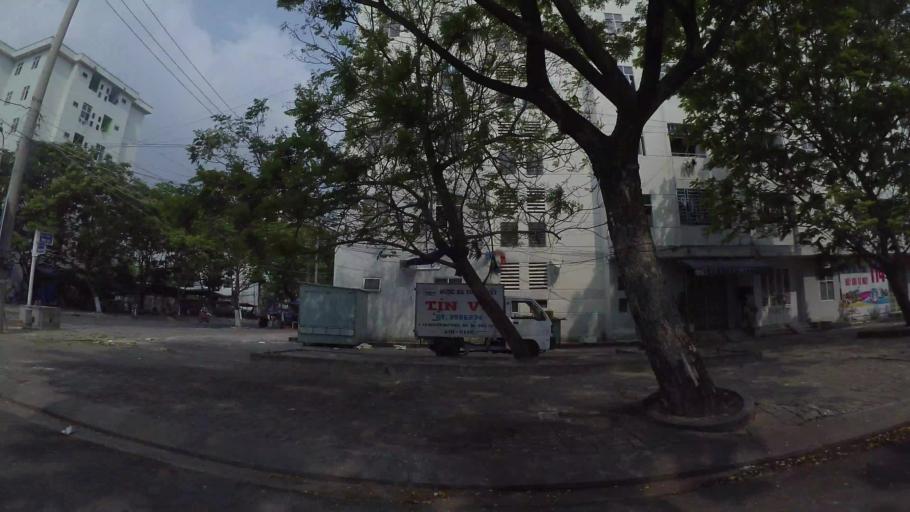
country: VN
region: Da Nang
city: Da Nang
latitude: 16.0961
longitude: 108.2291
